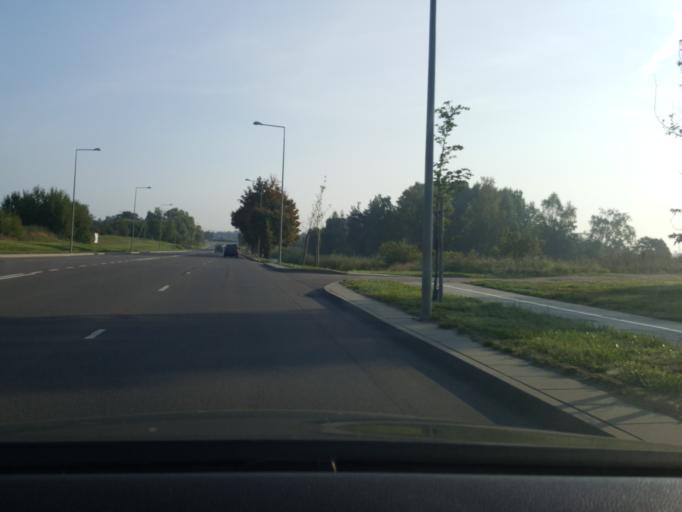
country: LT
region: Alytaus apskritis
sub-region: Alytus
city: Alytus
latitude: 54.4204
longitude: 24.0281
